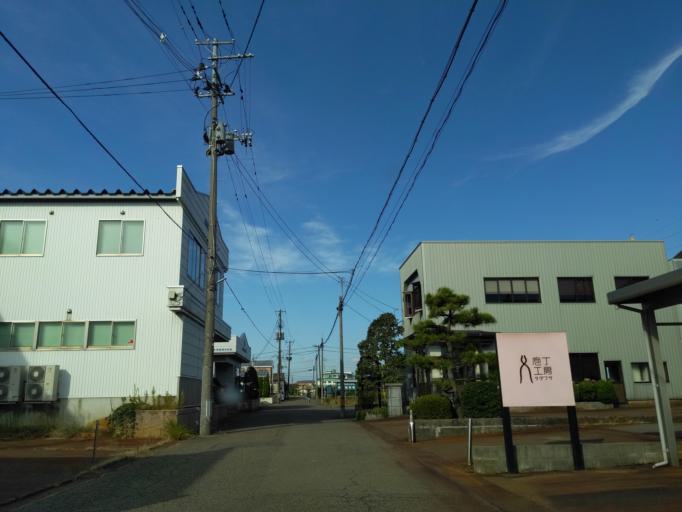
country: JP
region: Niigata
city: Sanjo
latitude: 37.6138
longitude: 138.9439
